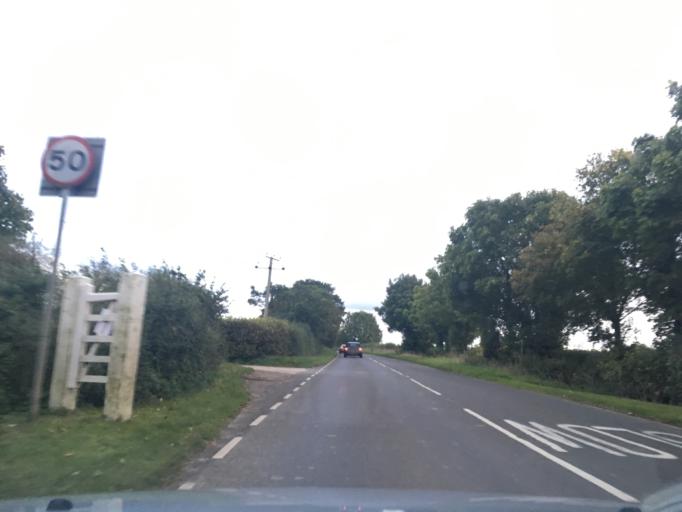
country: GB
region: England
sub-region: Oxfordshire
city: Kidlington
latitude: 51.8199
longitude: -1.2345
